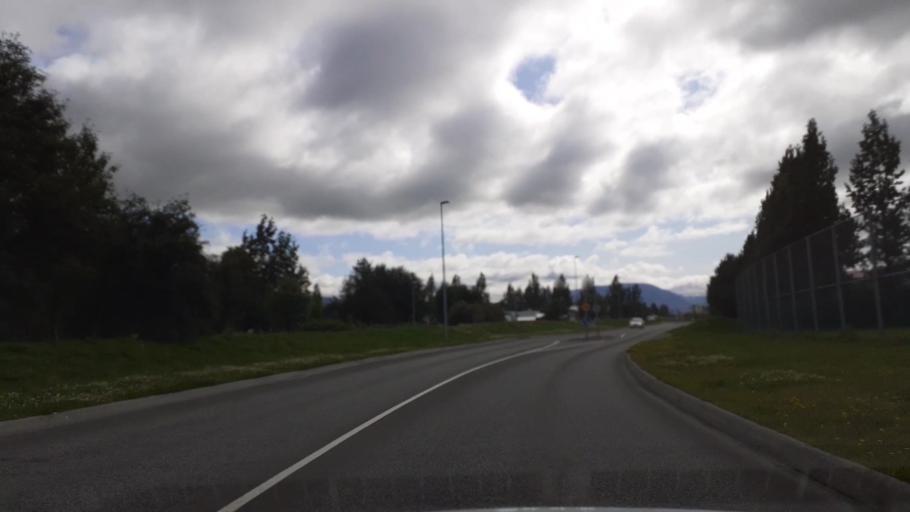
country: IS
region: Northeast
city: Akureyri
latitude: 65.6762
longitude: -18.1108
